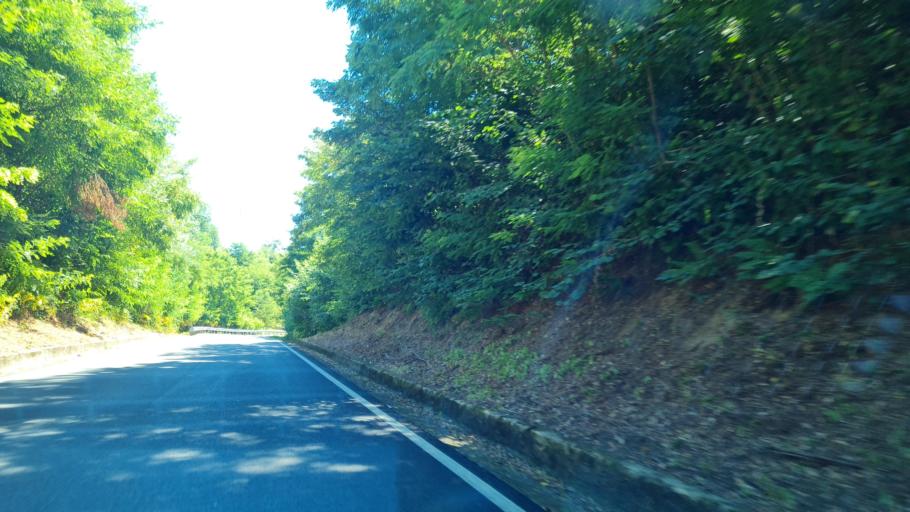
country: IT
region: Piedmont
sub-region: Provincia di Biella
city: Masserano
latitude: 45.5959
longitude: 8.2072
